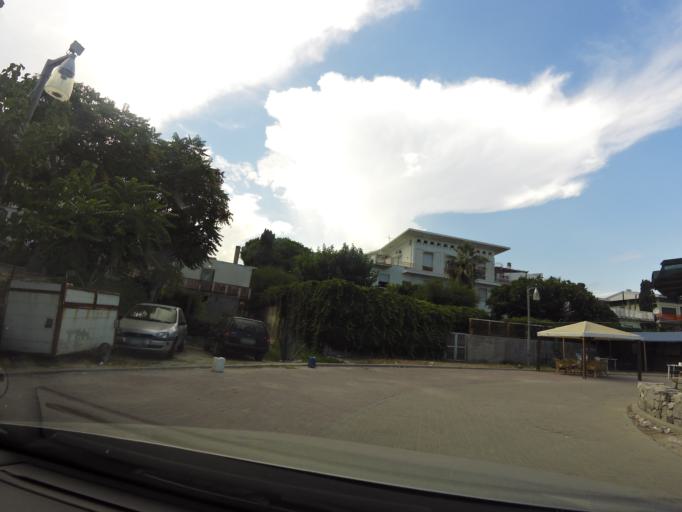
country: IT
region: Calabria
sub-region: Provincia di Reggio Calabria
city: Monasterace Marina
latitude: 38.4427
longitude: 16.5782
